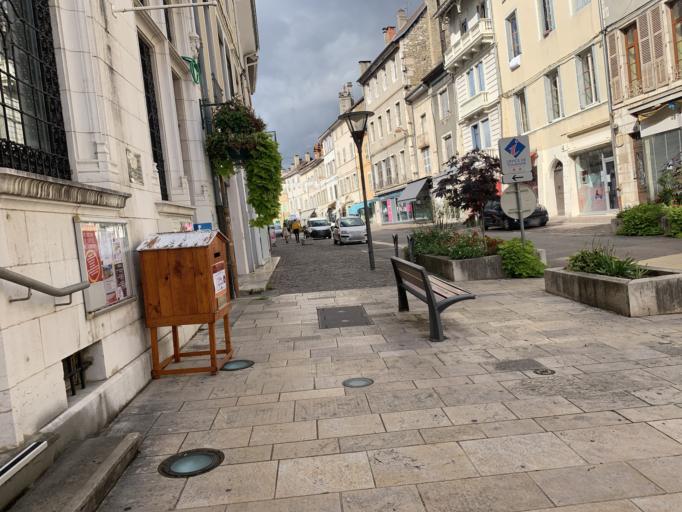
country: FR
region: Rhone-Alpes
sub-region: Departement de l'Ain
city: Belley
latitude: 45.7599
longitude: 5.6880
